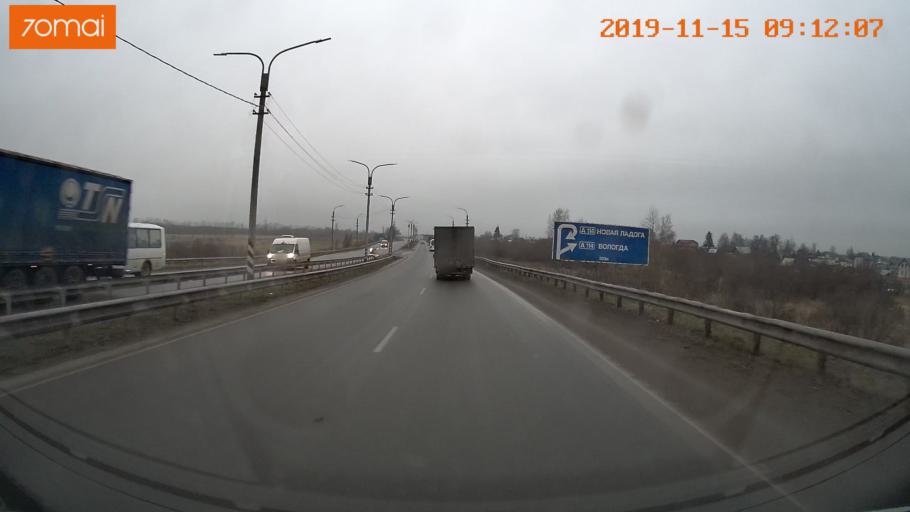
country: RU
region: Vologda
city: Tonshalovo
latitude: 59.2060
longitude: 37.9389
